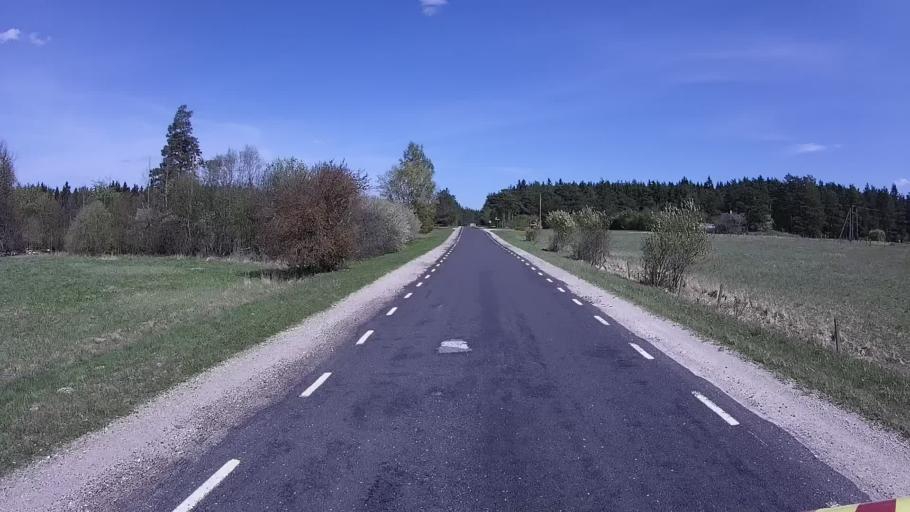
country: EE
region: Laeaene
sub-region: Ridala Parish
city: Uuemoisa
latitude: 59.0308
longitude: 23.8187
